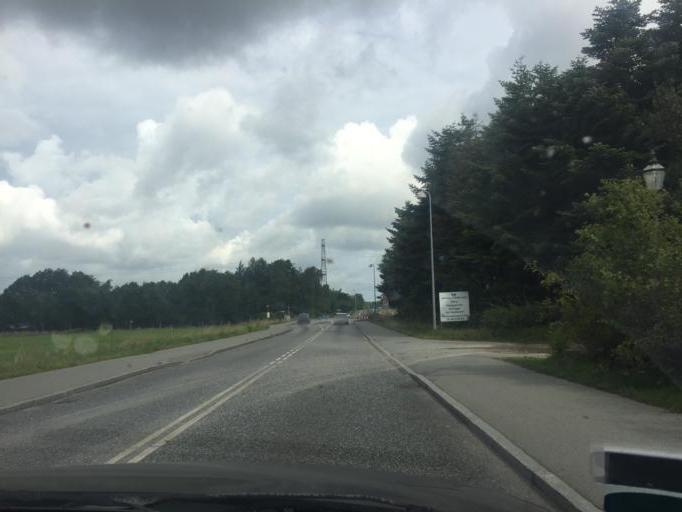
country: DK
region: Capital Region
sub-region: Allerod Kommune
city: Lillerod
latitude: 55.8912
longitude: 12.3519
